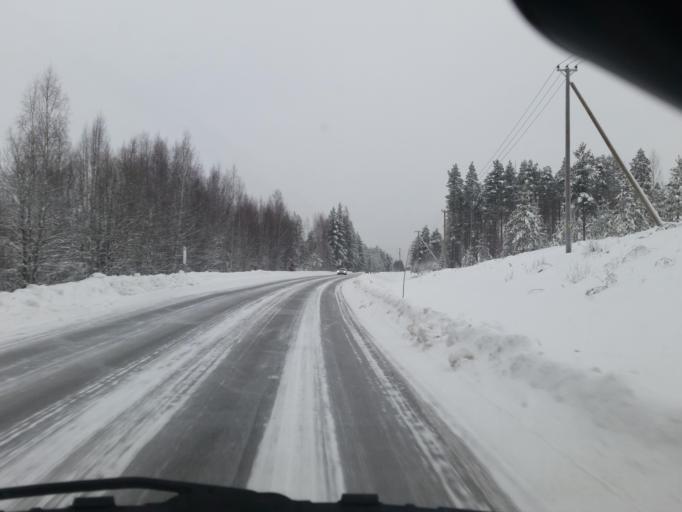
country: SE
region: Norrbotten
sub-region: Pitea Kommun
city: Bergsviken
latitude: 65.3878
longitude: 21.3241
